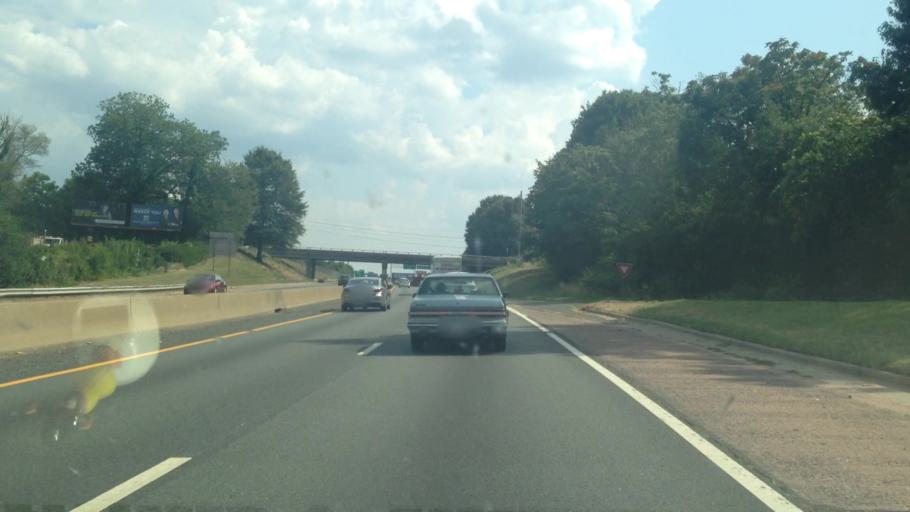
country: US
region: North Carolina
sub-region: Forsyth County
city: Winston-Salem
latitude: 36.1165
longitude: -80.2357
